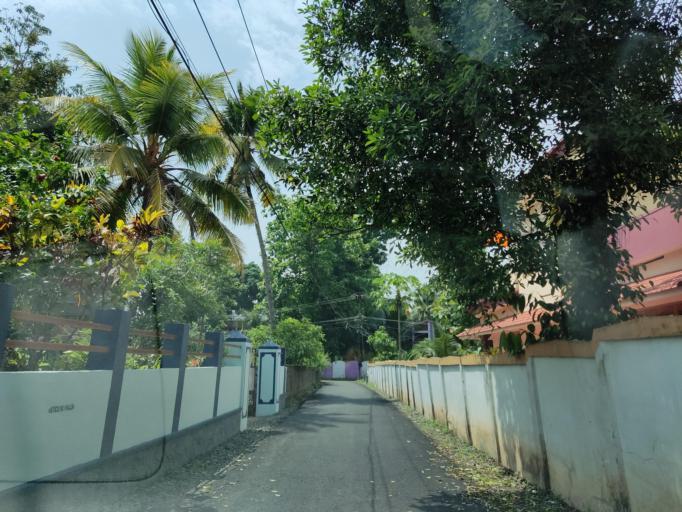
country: IN
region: Kerala
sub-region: Alappuzha
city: Chengannur
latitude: 9.3064
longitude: 76.5836
